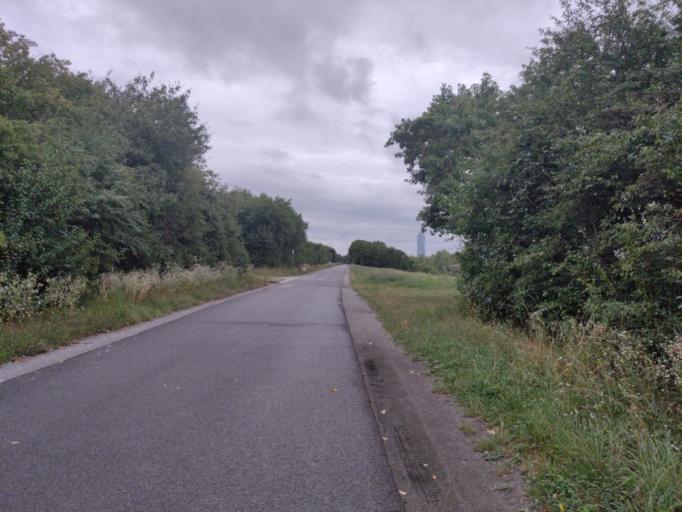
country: AT
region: Lower Austria
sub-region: Politischer Bezirk Korneuburg
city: Langenzersdorf
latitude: 48.2612
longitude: 16.3746
